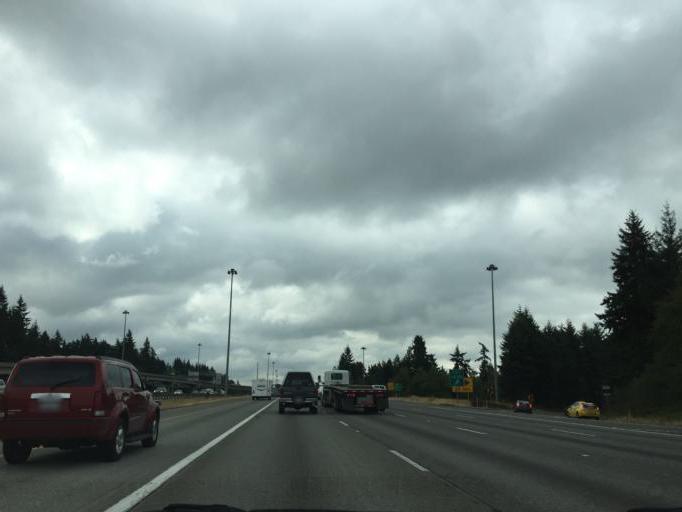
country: US
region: Washington
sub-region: King County
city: Lakeland South
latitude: 47.2925
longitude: -122.3059
